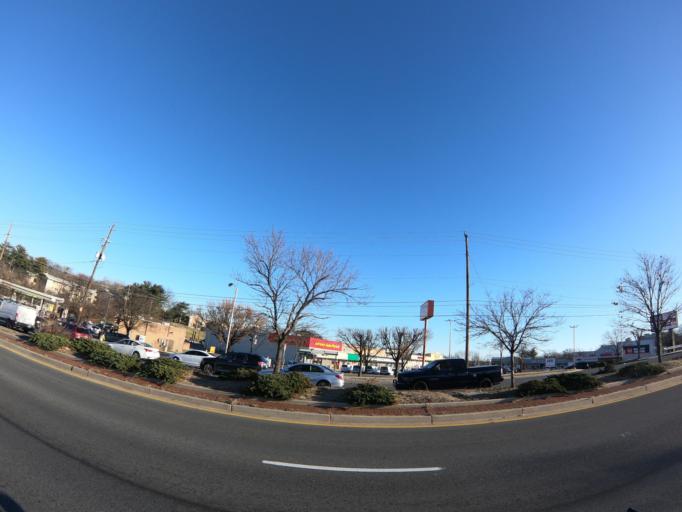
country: US
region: Maryland
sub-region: Prince George's County
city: Lanham
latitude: 38.9573
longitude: -76.8702
